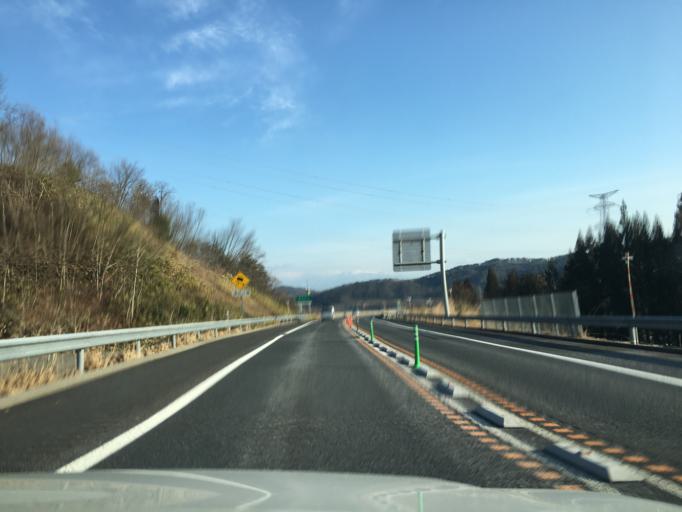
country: JP
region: Yamagata
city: Sagae
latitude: 38.4175
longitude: 140.1874
